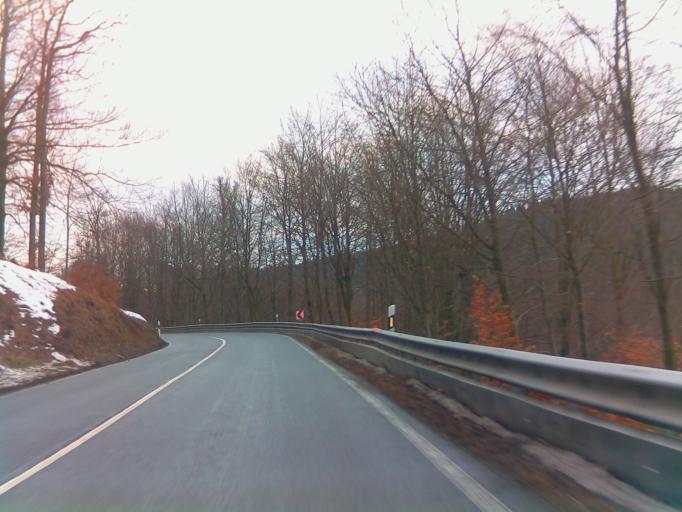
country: DE
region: Baden-Wuerttemberg
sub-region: Karlsruhe Region
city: Eberbach
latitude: 49.4558
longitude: 9.0268
